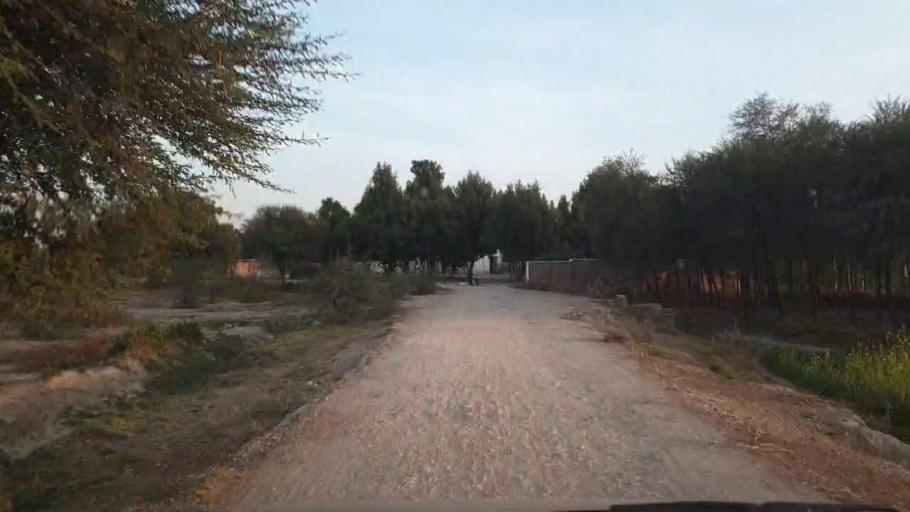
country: PK
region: Sindh
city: Chambar
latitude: 25.2818
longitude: 68.8180
